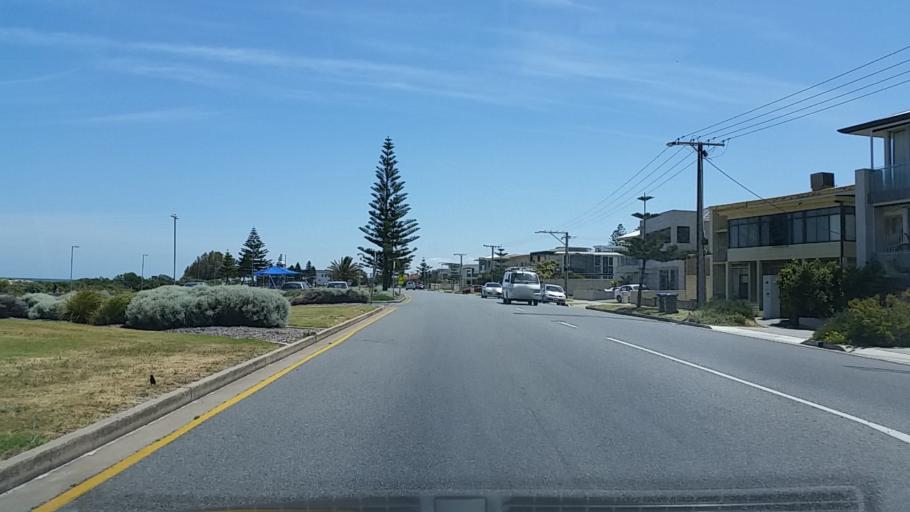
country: AU
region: South Australia
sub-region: Charles Sturt
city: Henley Beach
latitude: -34.9414
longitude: 138.5004
